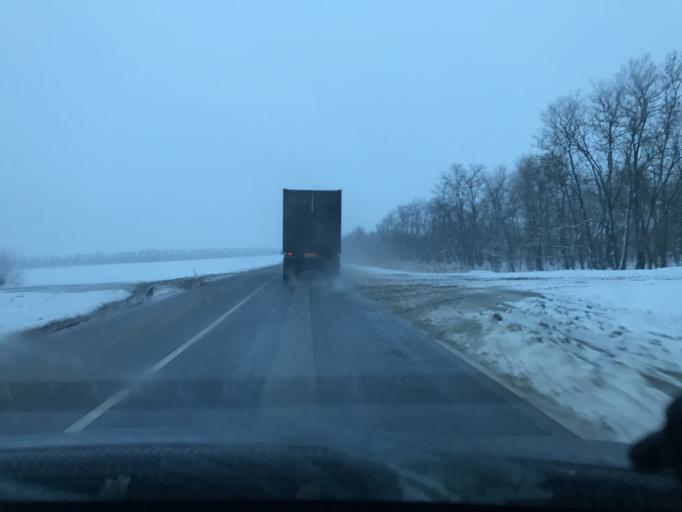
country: RU
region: Rostov
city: Letnik
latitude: 46.0736
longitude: 41.1986
